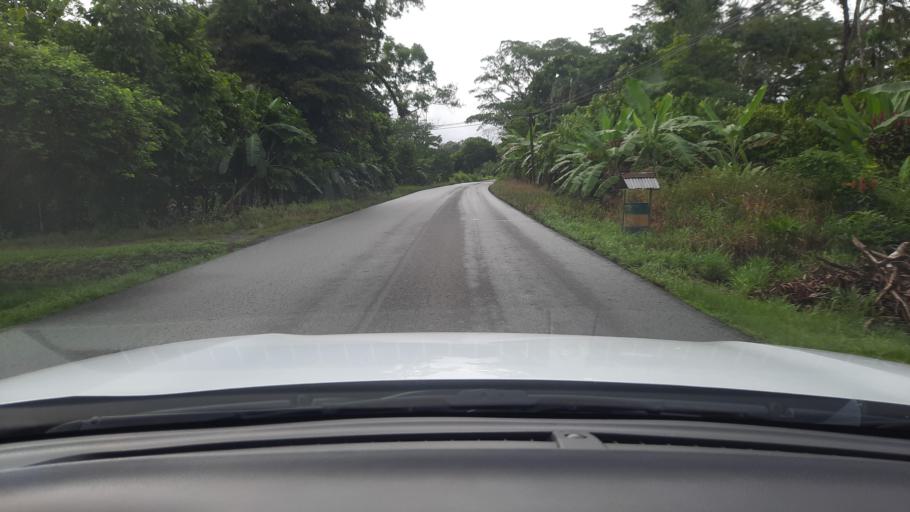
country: CR
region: Alajuela
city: Upala
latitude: 10.9247
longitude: -85.0709
